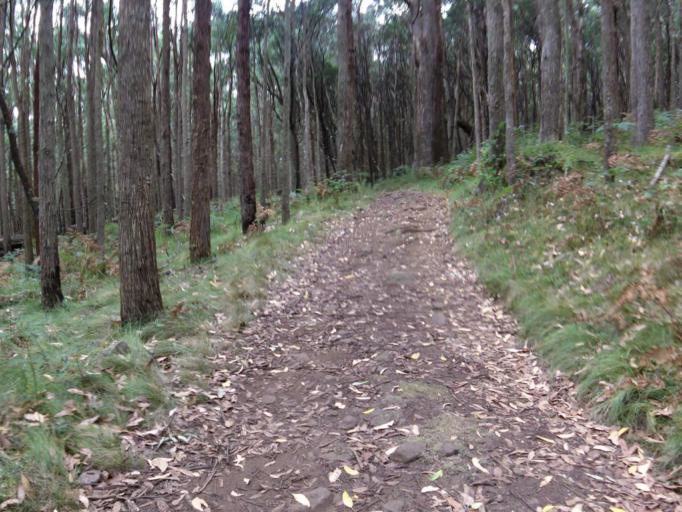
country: AU
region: Victoria
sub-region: Hume
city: Sunbury
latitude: -37.3812
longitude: 144.5734
